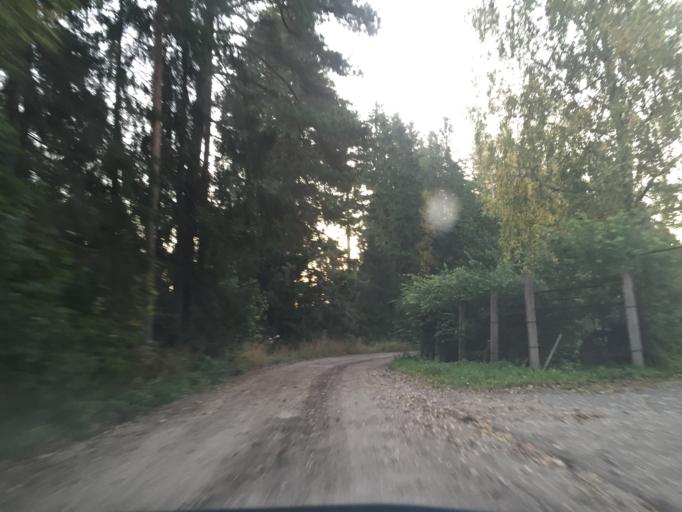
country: LV
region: Vecpiebalga
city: Vecpiebalga
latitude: 57.0681
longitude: 25.7454
